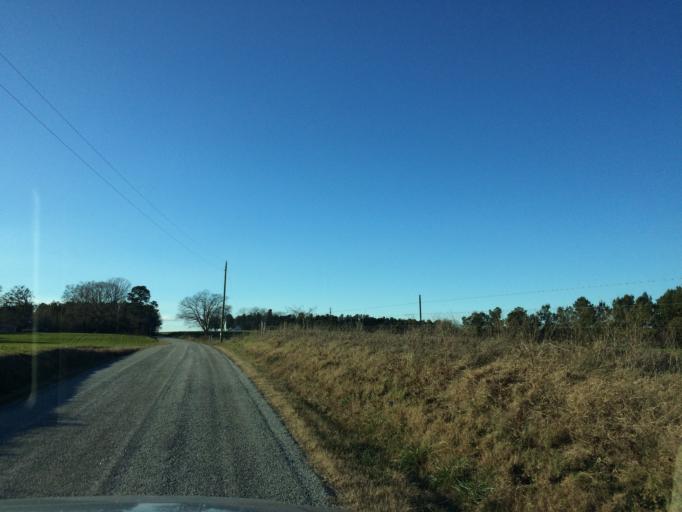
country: US
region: Georgia
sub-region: Hart County
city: Hartwell
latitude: 34.3672
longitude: -83.0234
